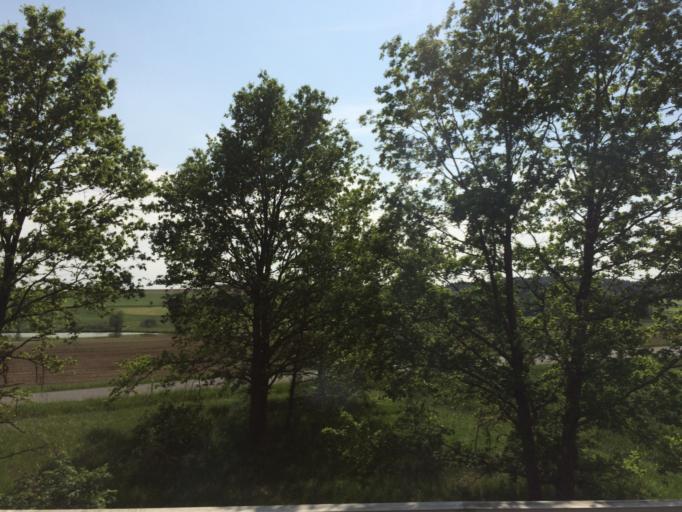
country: DE
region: Bavaria
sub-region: Regierungsbezirk Mittelfranken
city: Emskirchen
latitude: 49.5565
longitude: 10.6989
